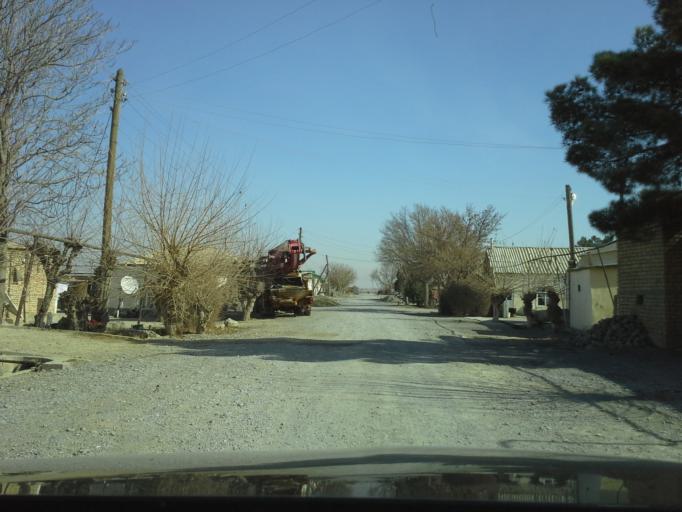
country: TM
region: Ahal
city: Arcabil
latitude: 38.1060
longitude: 57.9809
